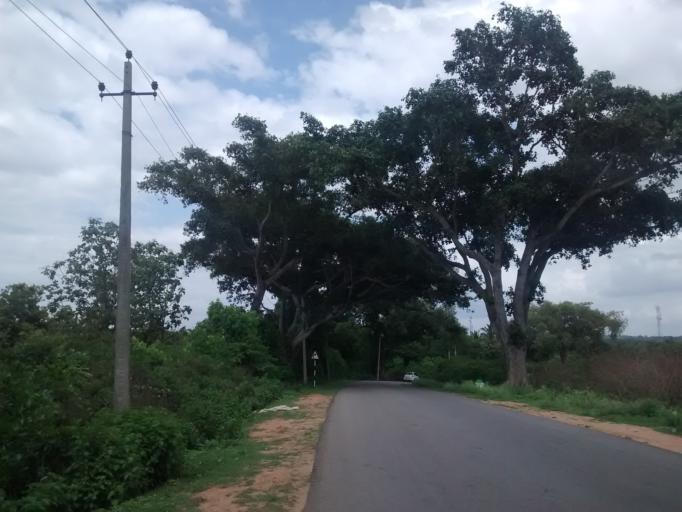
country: IN
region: Karnataka
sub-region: Tumkur
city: Kunigal
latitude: 13.1148
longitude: 77.1578
